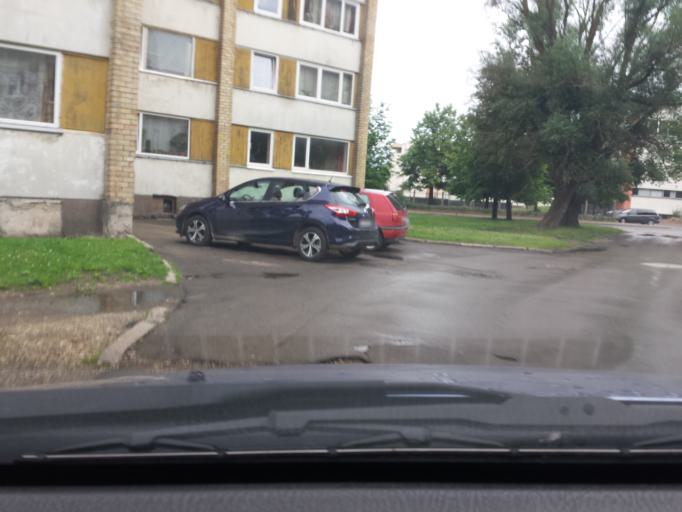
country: LV
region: Kekava
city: Kekava
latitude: 56.9028
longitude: 24.2064
